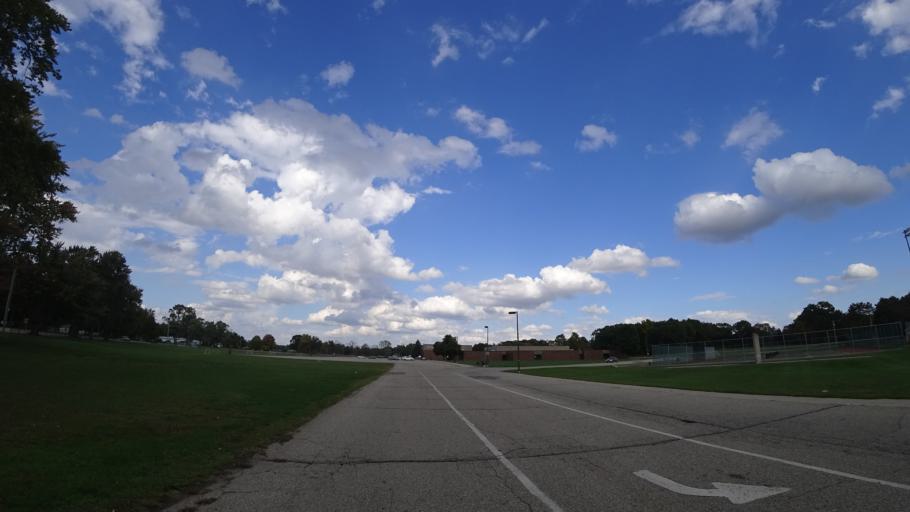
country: US
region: Michigan
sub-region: Saint Joseph County
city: Three Rivers
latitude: 41.9512
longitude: -85.6197
